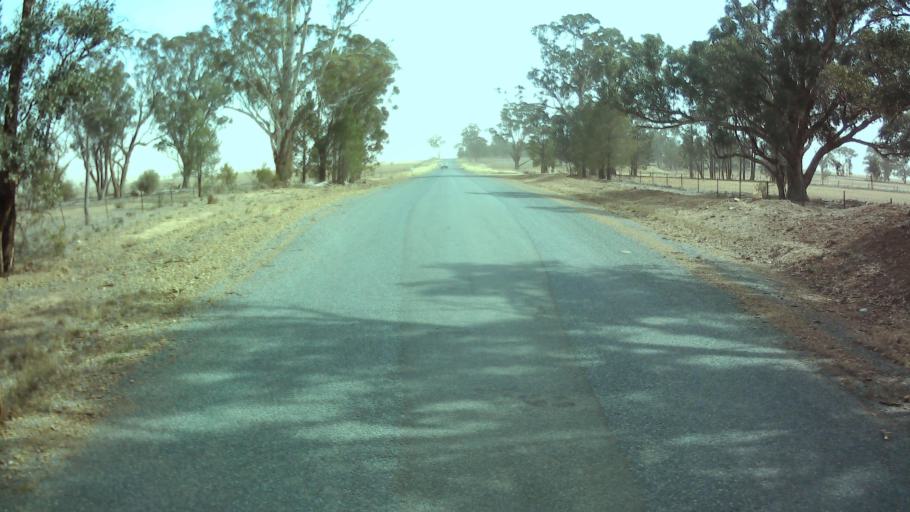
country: AU
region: New South Wales
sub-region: Weddin
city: Grenfell
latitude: -33.7514
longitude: 147.9906
